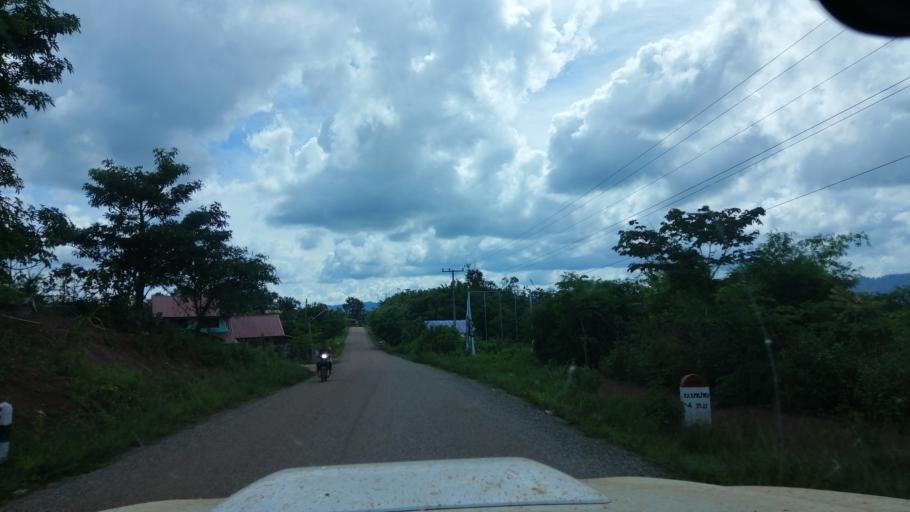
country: TH
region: Uttaradit
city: Ban Khok
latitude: 18.3675
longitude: 101.1448
